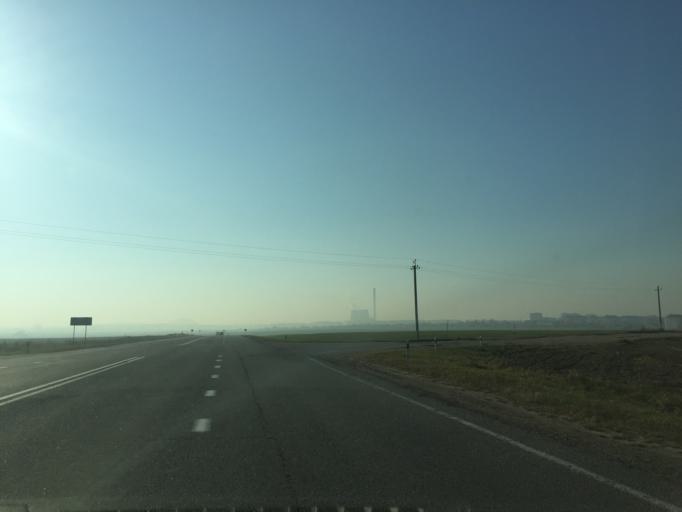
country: BY
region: Gomel
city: Kastsyukowka
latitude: 52.4779
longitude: 30.8215
